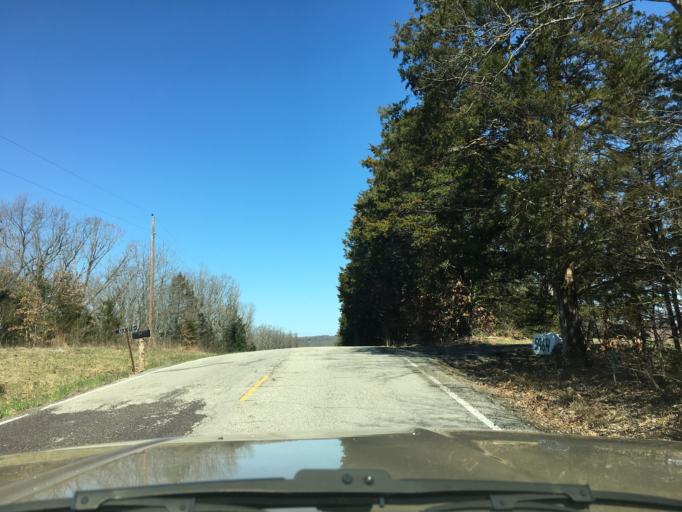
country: US
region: Missouri
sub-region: Franklin County
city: Gerald
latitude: 38.5188
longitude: -91.3269
